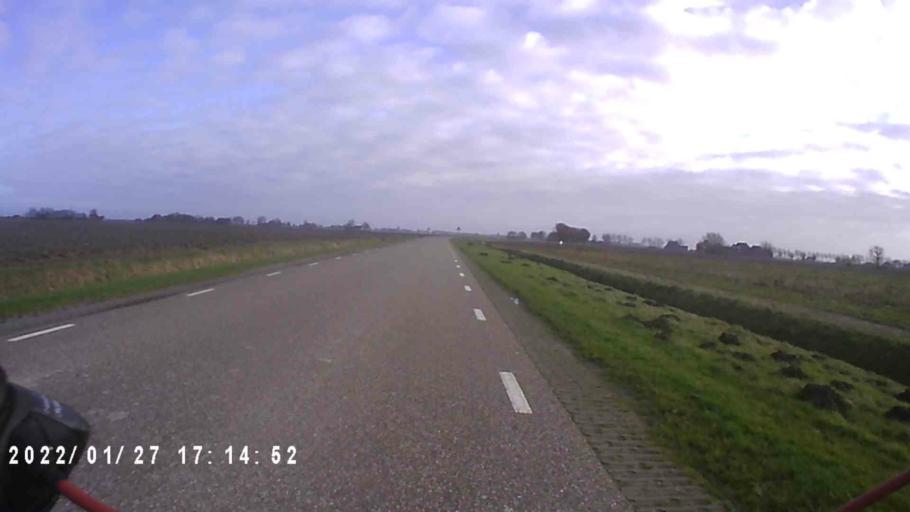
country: NL
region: Friesland
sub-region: Gemeente Dongeradeel
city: Anjum
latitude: 53.3947
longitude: 6.0958
